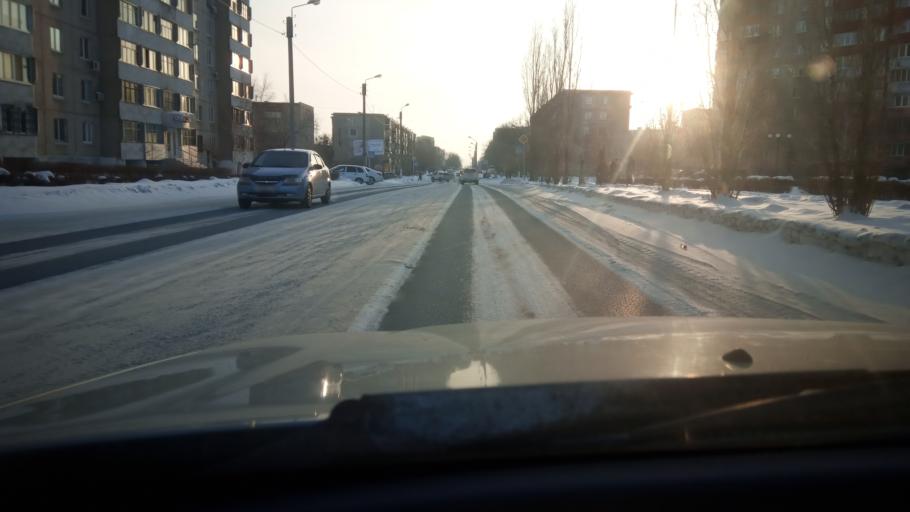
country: RU
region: Orenburg
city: Novotroitsk
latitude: 51.1902
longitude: 58.2818
